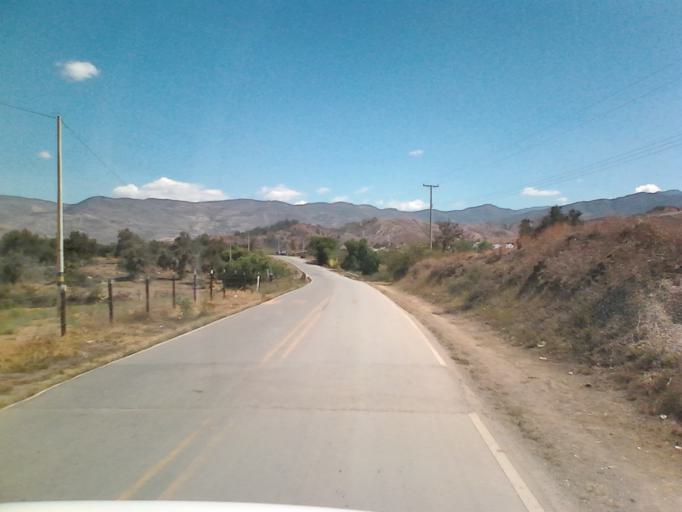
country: CO
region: Boyaca
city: Villa de Leiva
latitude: 5.6107
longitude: -73.5644
